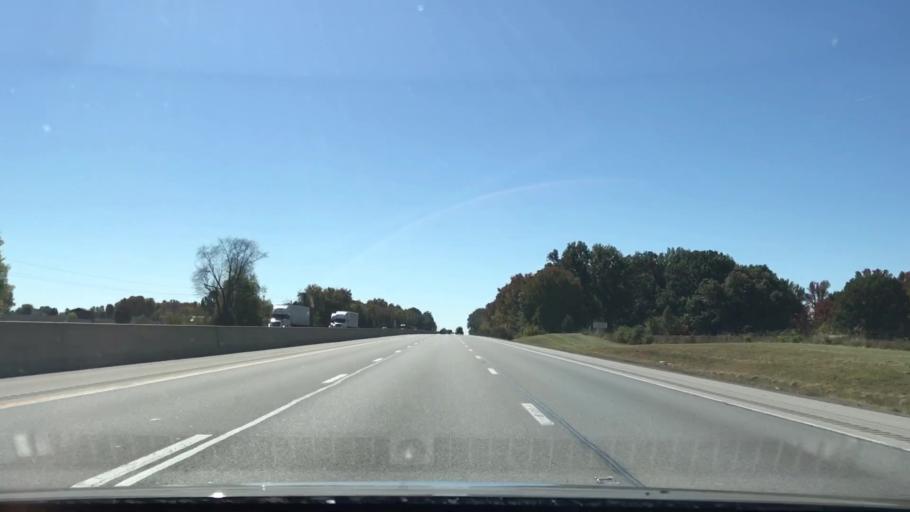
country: US
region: Kentucky
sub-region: Warren County
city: Plano
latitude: 36.8609
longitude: -86.4538
